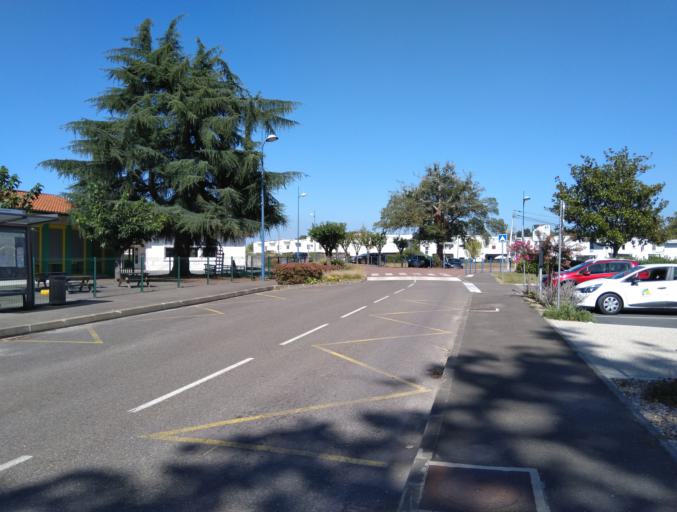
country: FR
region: Aquitaine
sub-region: Departement des Landes
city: Narrosse
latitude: 43.6931
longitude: -1.0087
